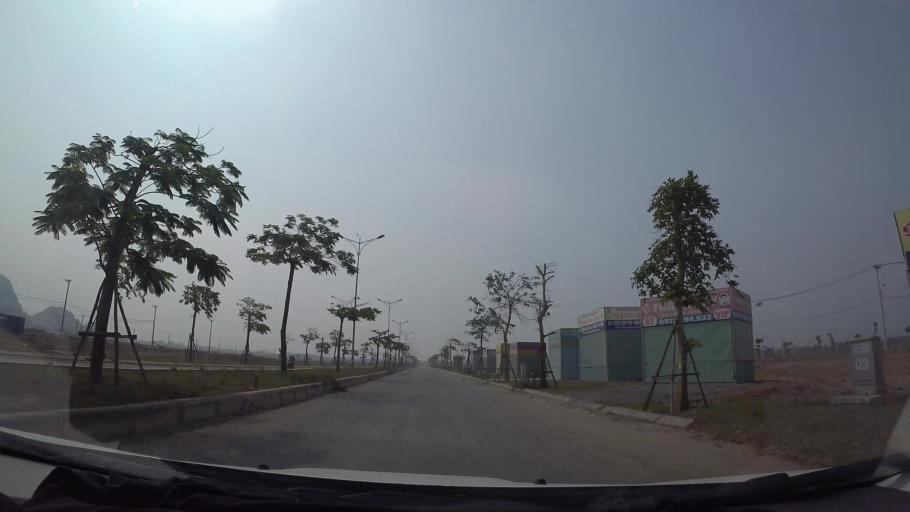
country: VN
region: Da Nang
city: Ngu Hanh Son
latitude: 16.0028
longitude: 108.2466
